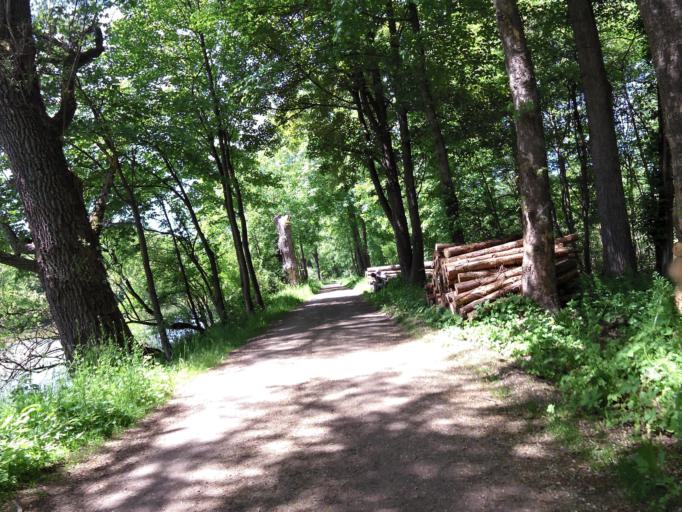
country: DE
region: Bavaria
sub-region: Upper Bavaria
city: Marzling
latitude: 48.4040
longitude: 11.7815
